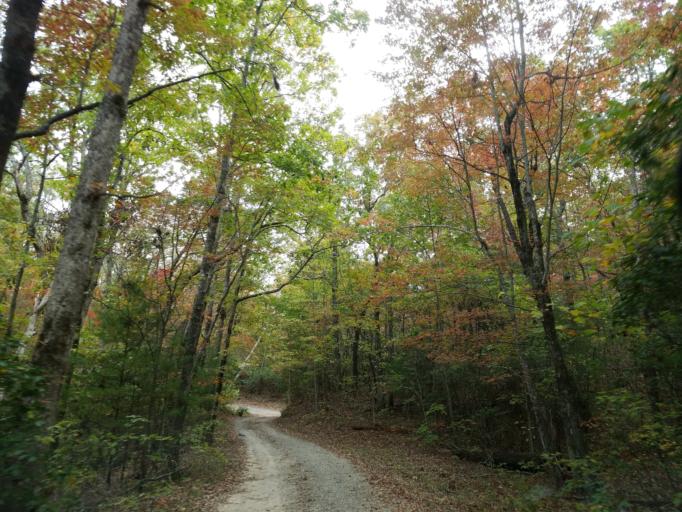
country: US
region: Georgia
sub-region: Dawson County
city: Dawsonville
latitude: 34.5857
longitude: -84.2345
